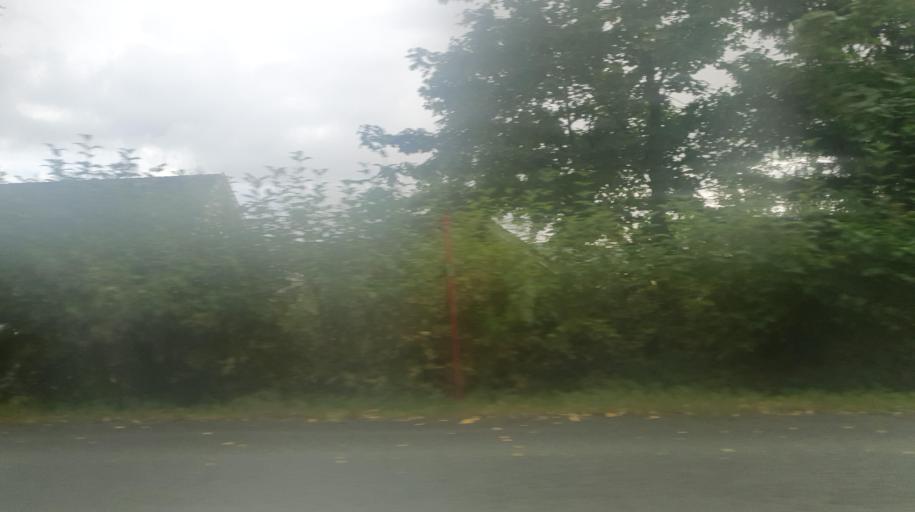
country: NO
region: Nord-Trondelag
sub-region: Verdal
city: Verdal
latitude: 63.7943
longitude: 11.5383
